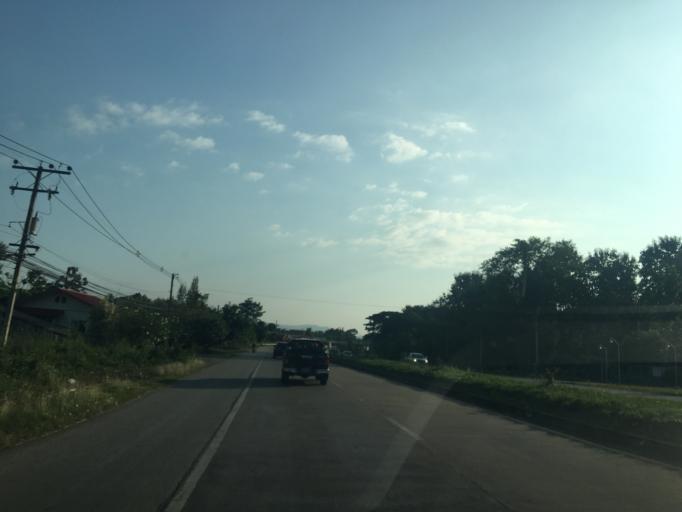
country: TH
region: Lampang
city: Ngao
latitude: 18.7323
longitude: 99.9708
